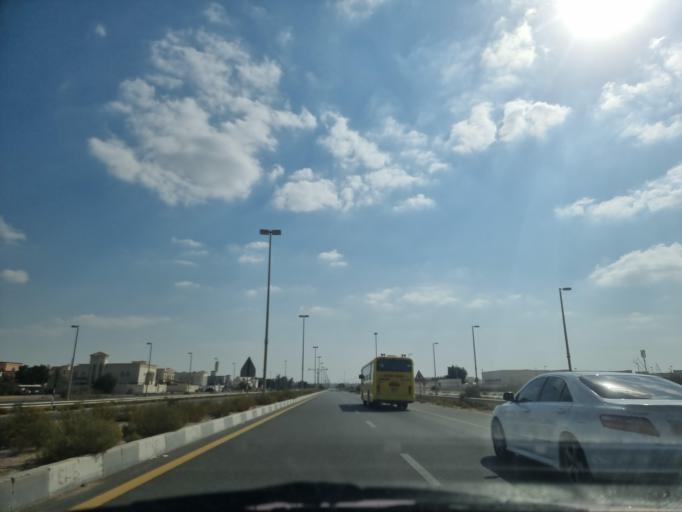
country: AE
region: Abu Dhabi
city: Abu Dhabi
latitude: 24.4122
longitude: 54.7330
